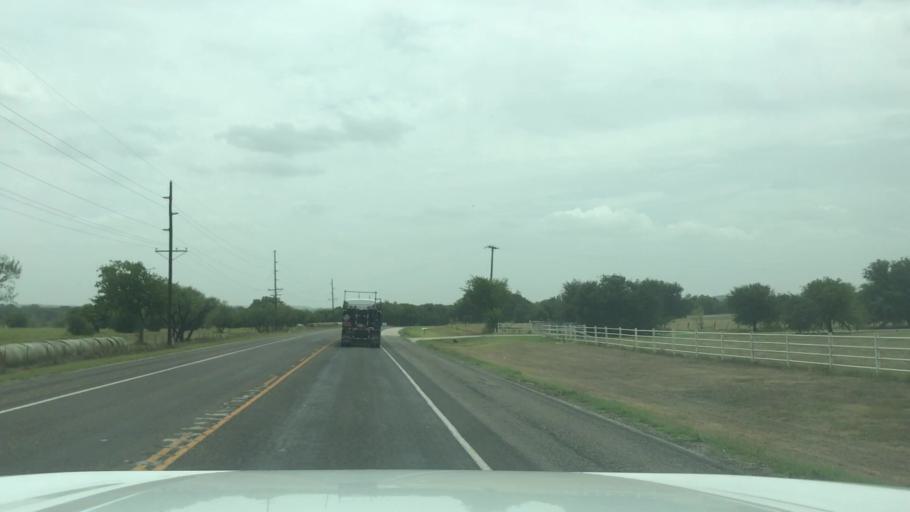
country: US
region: Texas
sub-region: Bosque County
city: Clifton
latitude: 31.7495
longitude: -97.5556
